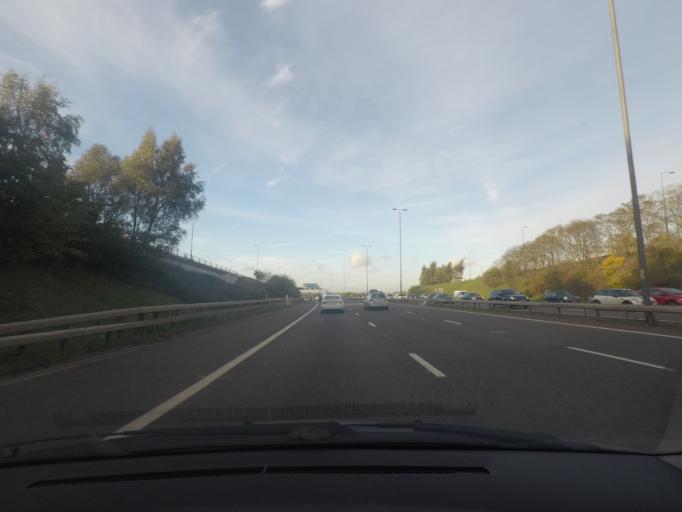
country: GB
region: England
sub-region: City and Borough of Leeds
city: Lofthouse
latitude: 53.7330
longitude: -1.5115
